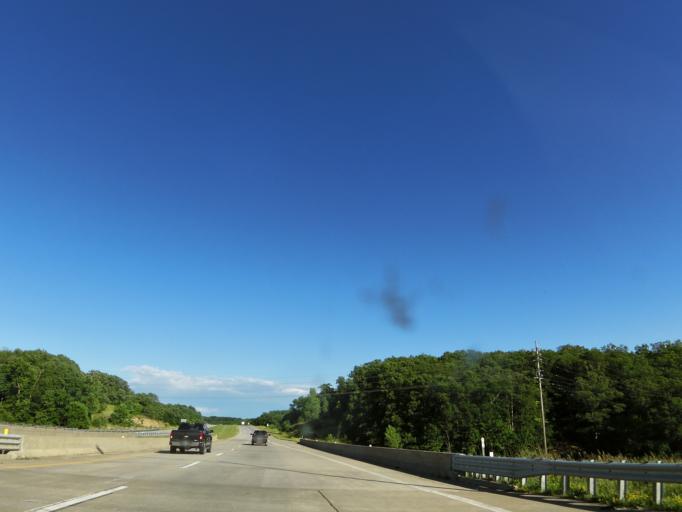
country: US
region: Missouri
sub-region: Pike County
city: Bowling Green
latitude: 39.3559
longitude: -91.1992
